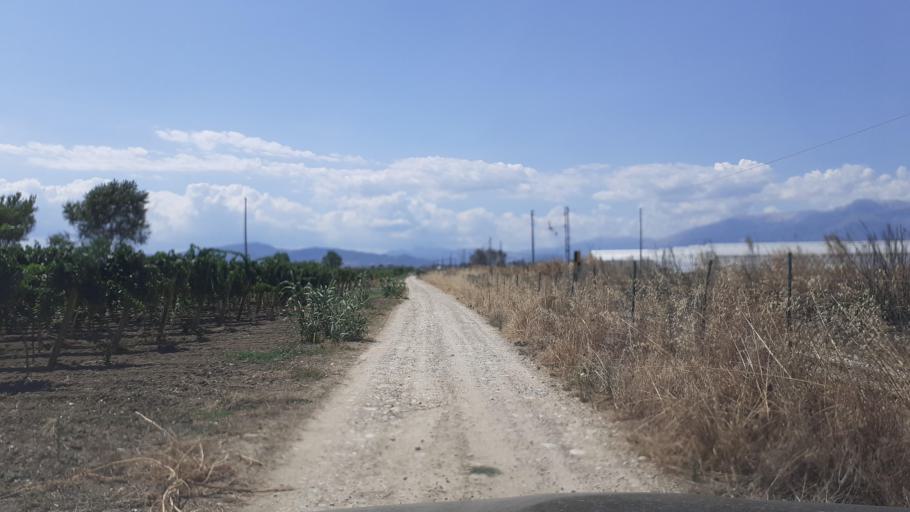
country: IT
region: Abruzzo
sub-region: Provincia di Chieti
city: Fossacesia
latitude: 42.2062
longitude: 14.4927
